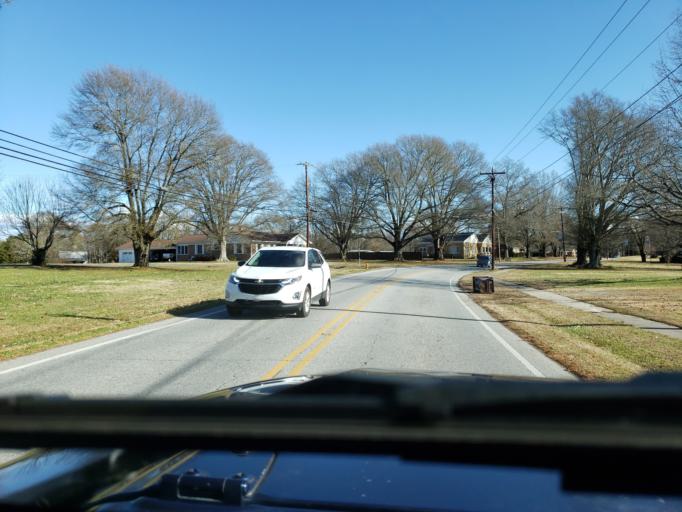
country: US
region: North Carolina
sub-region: Cleveland County
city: White Plains
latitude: 35.1769
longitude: -81.4534
